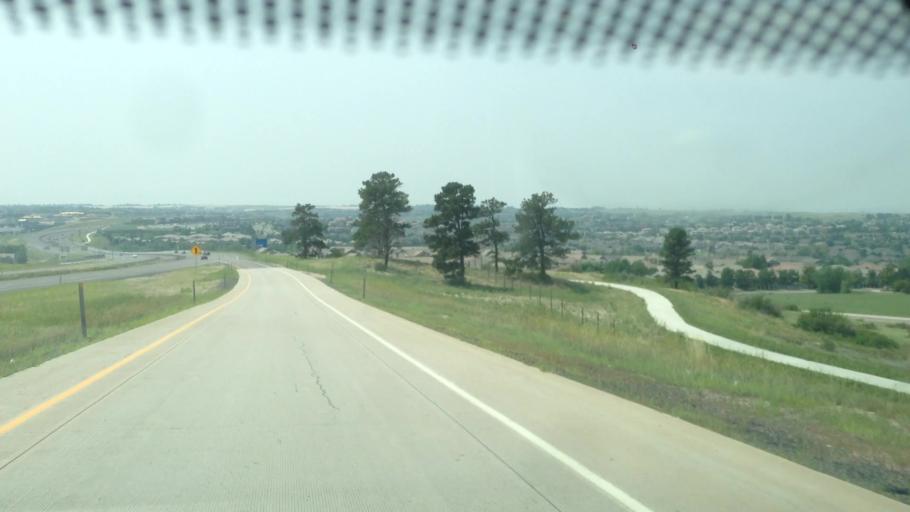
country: US
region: Colorado
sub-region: Douglas County
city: Parker
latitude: 39.5976
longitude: -104.7169
